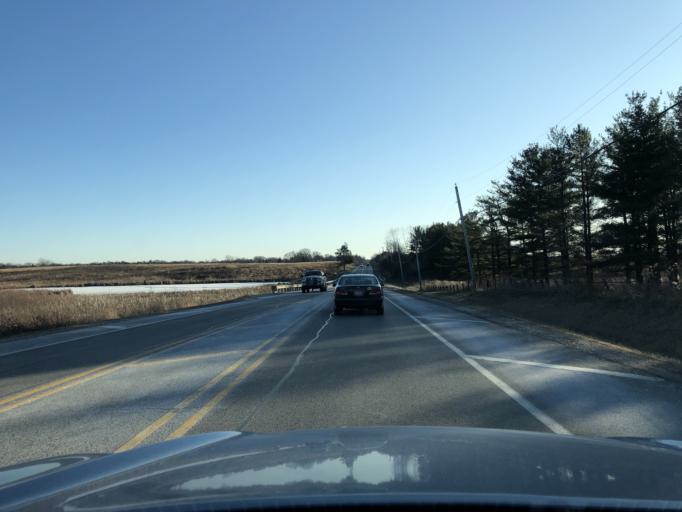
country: US
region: Illinois
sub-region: Lake County
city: Lake Zurich
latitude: 42.1744
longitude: -88.1017
